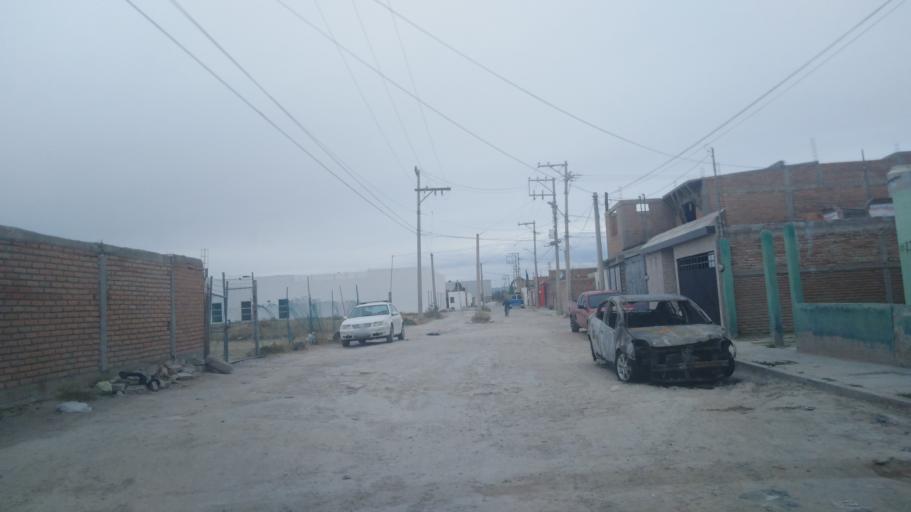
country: MX
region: Durango
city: Victoria de Durango
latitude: 24.0226
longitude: -104.6163
